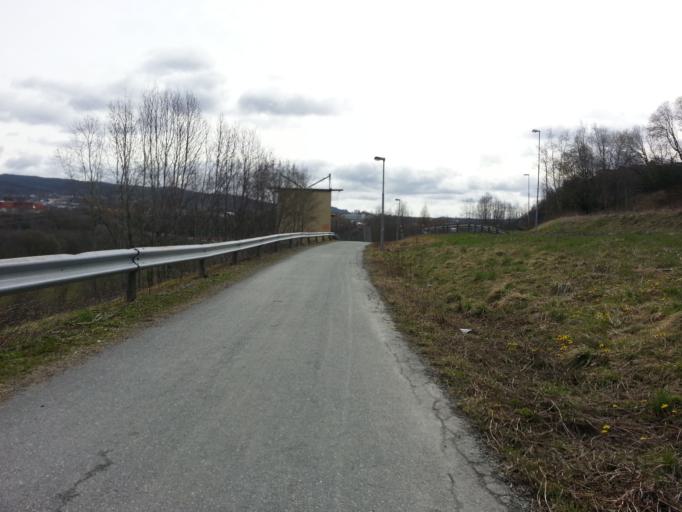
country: NO
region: Sor-Trondelag
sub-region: Trondheim
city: Trondheim
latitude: 63.4087
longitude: 10.3851
